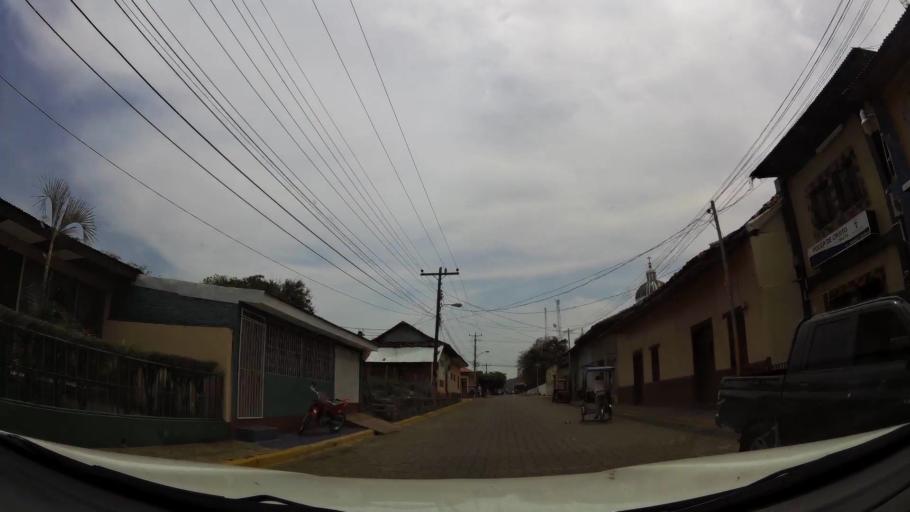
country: NI
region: Rivas
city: Rivas
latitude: 11.4392
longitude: -85.8266
